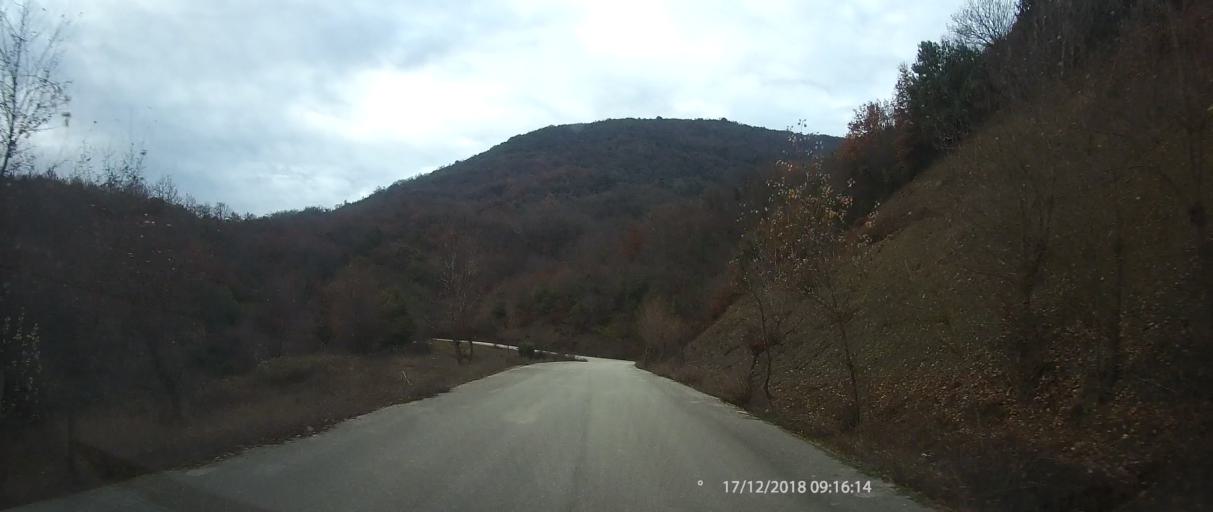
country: GR
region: Epirus
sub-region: Nomos Ioanninon
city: Kalpaki
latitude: 39.9620
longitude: 20.6568
